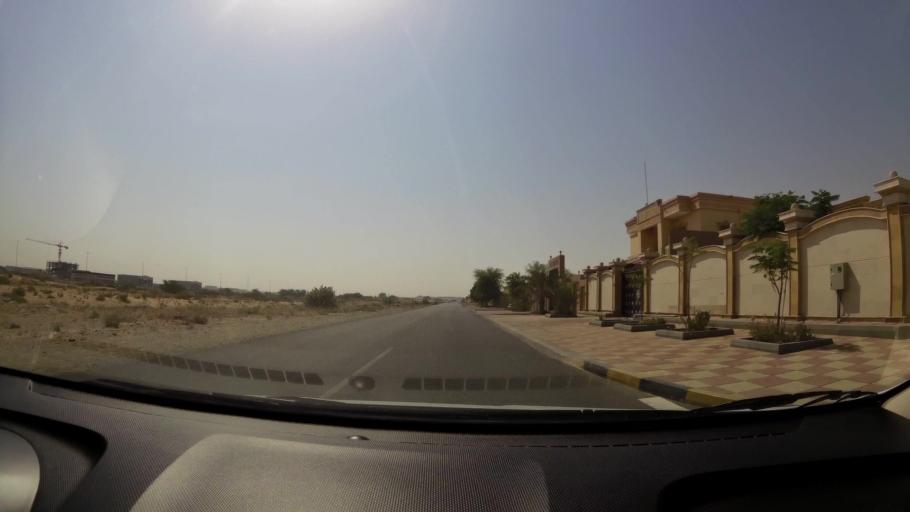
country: AE
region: Ajman
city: Ajman
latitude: 25.4175
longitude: 55.5401
